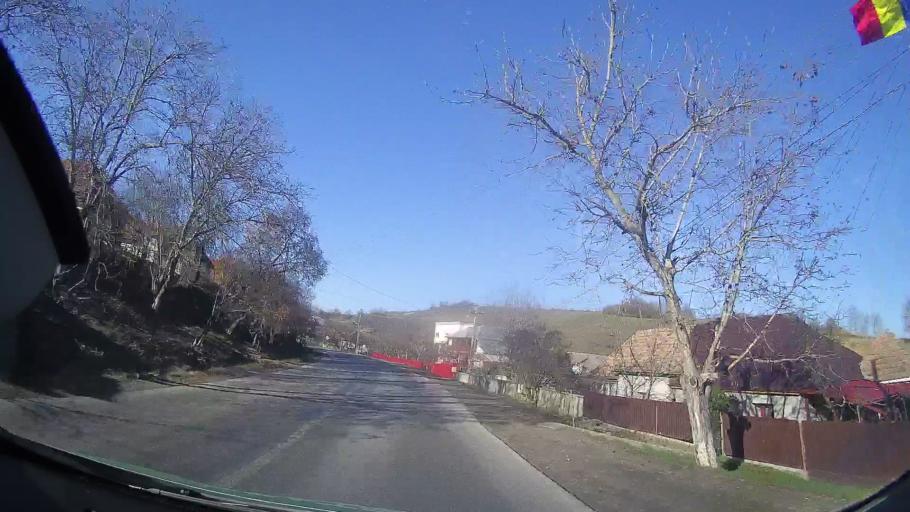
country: RO
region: Mures
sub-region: Comuna Sarmasu
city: Sarmasu
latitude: 46.7862
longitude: 24.2038
